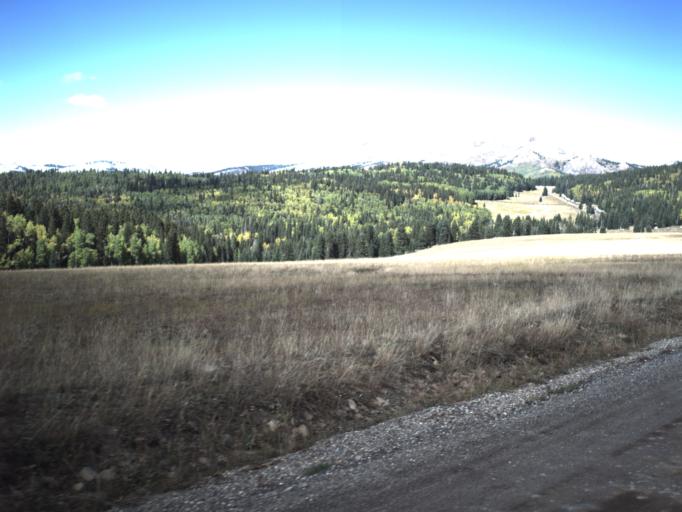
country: US
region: Utah
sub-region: Piute County
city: Junction
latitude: 38.2785
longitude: -112.3623
